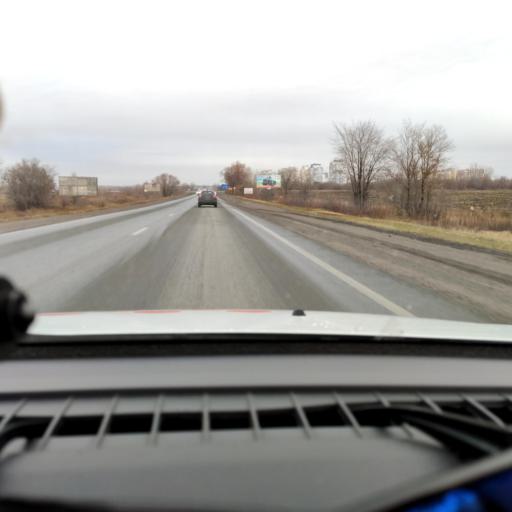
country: RU
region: Samara
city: Samara
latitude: 53.0882
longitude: 50.1460
